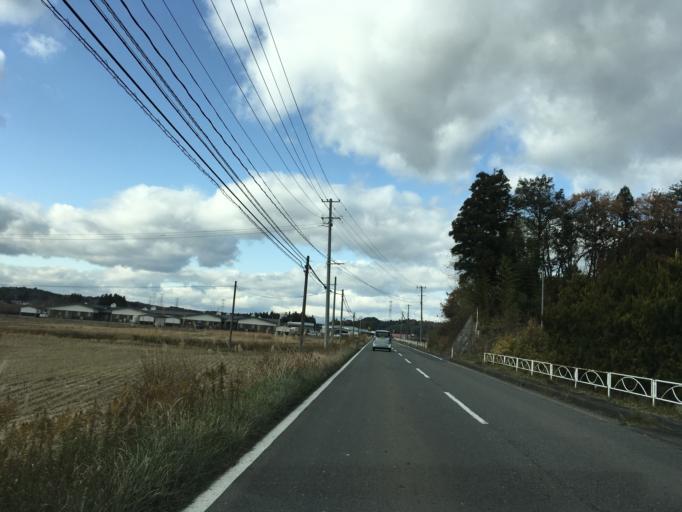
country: JP
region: Iwate
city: Ichinoseki
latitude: 38.8557
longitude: 141.1669
